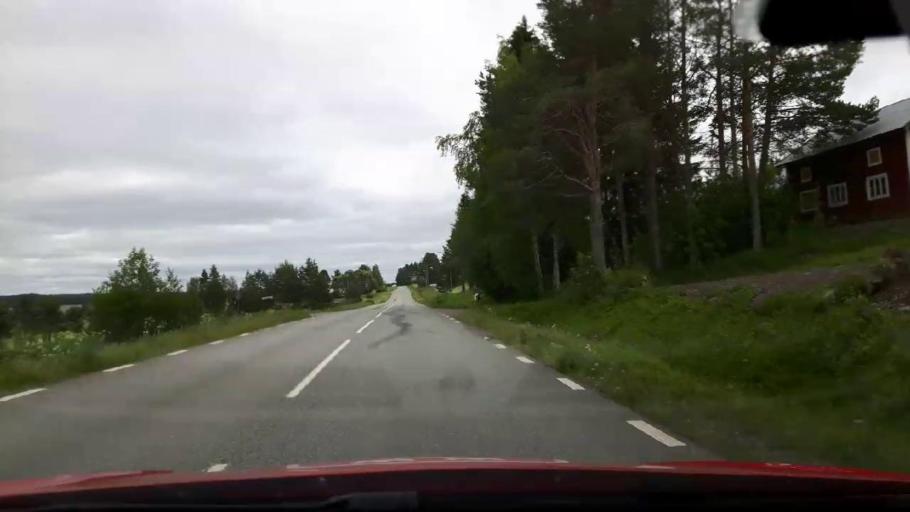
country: SE
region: Jaemtland
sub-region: Stroemsunds Kommun
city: Stroemsund
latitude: 63.5652
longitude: 15.3942
